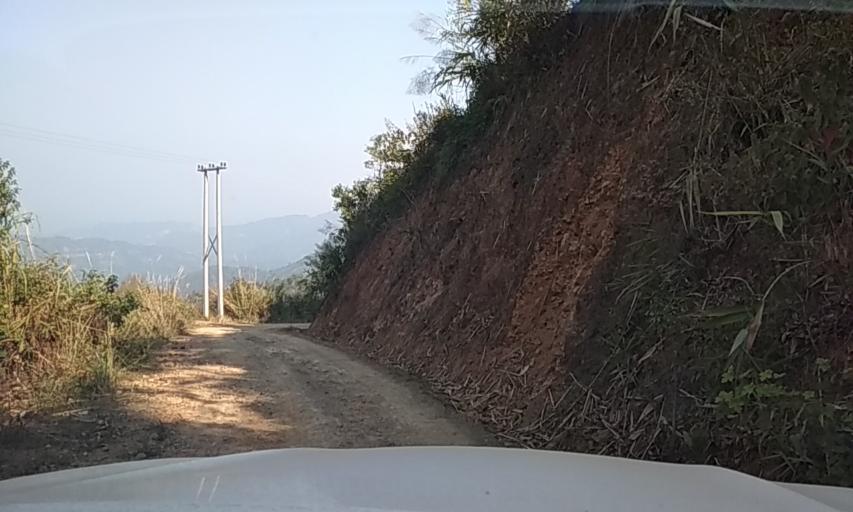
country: LA
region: Phongsali
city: Phongsali
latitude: 21.6871
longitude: 102.1010
